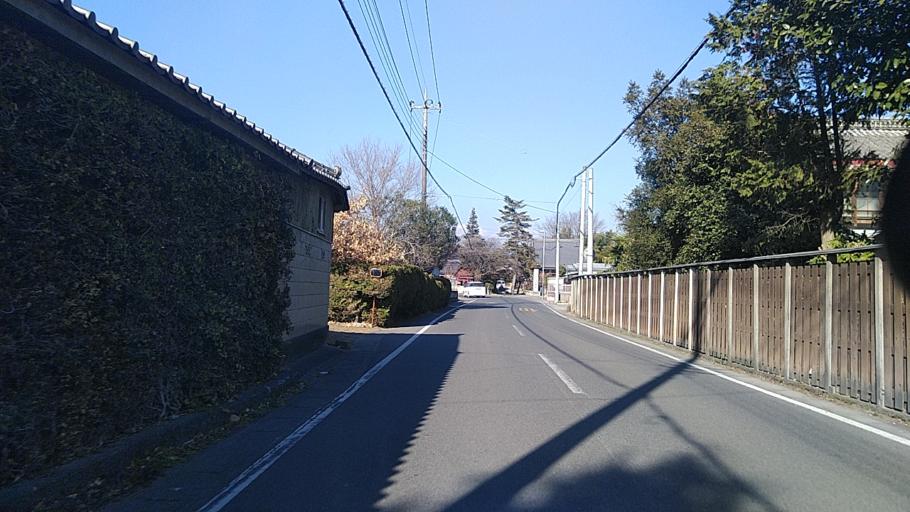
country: JP
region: Tochigi
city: Tanuma
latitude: 36.3588
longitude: 139.5615
